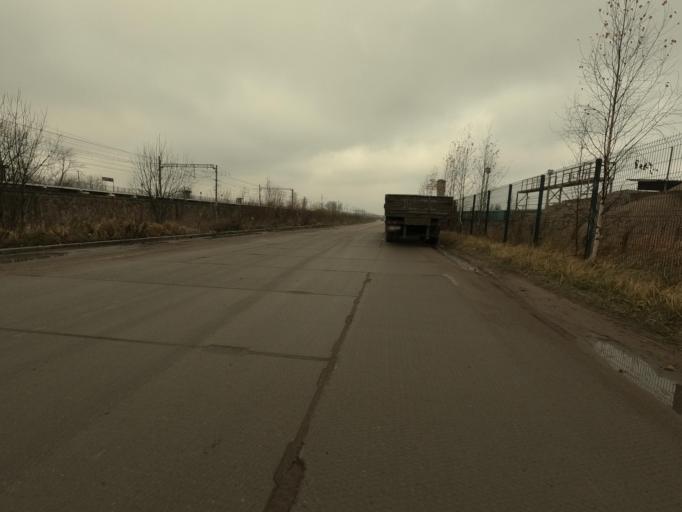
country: RU
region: Leningrad
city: Lyuban'
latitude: 59.4685
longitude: 31.2537
